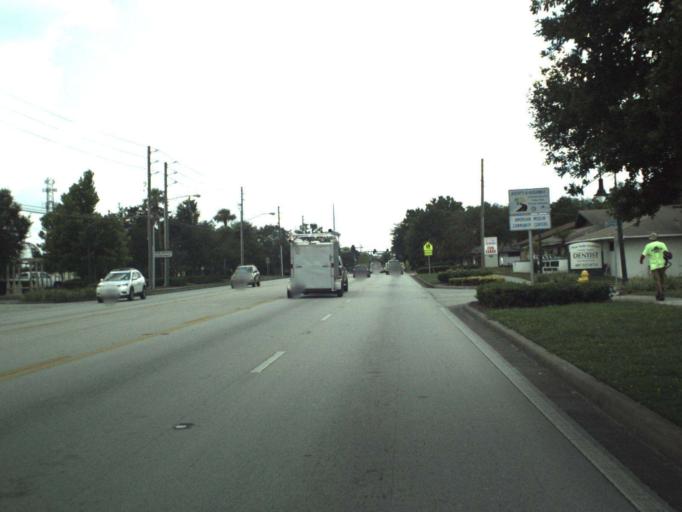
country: US
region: Florida
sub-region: Seminole County
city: Winter Springs
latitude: 28.6983
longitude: -81.3109
